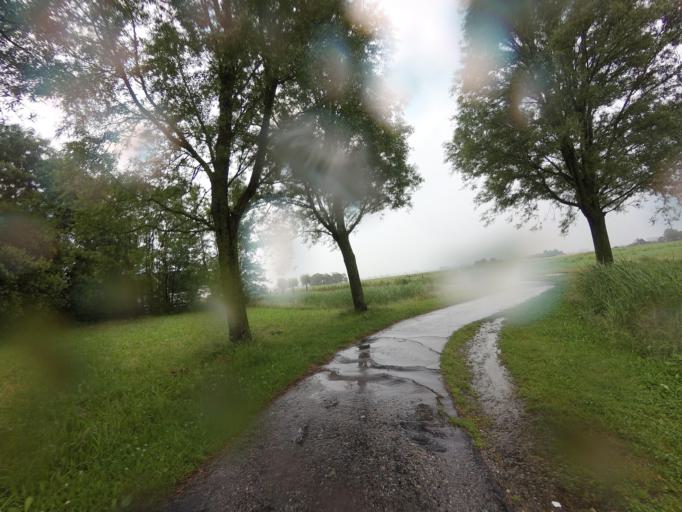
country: NL
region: North Holland
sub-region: Gemeente Schagen
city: Schagen
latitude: 52.7737
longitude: 4.8058
